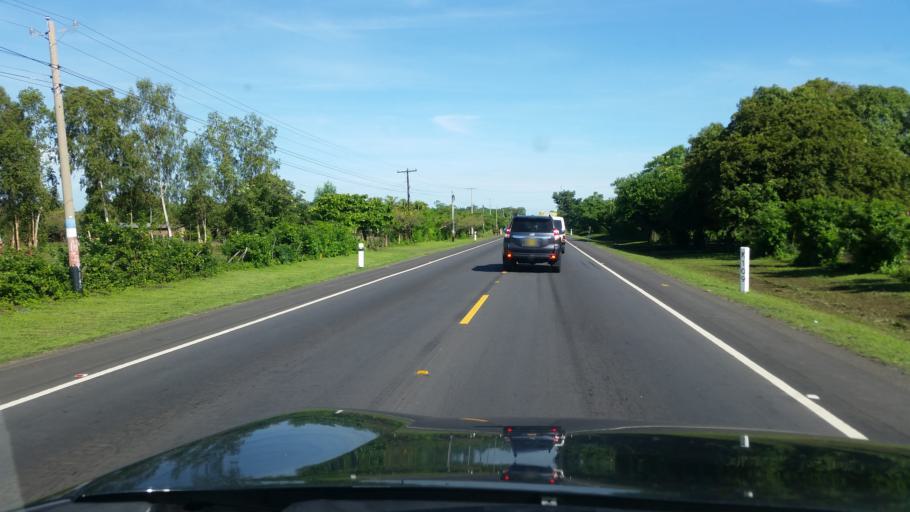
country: NI
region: Leon
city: Quezalguaque
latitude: 12.5478
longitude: -86.9283
